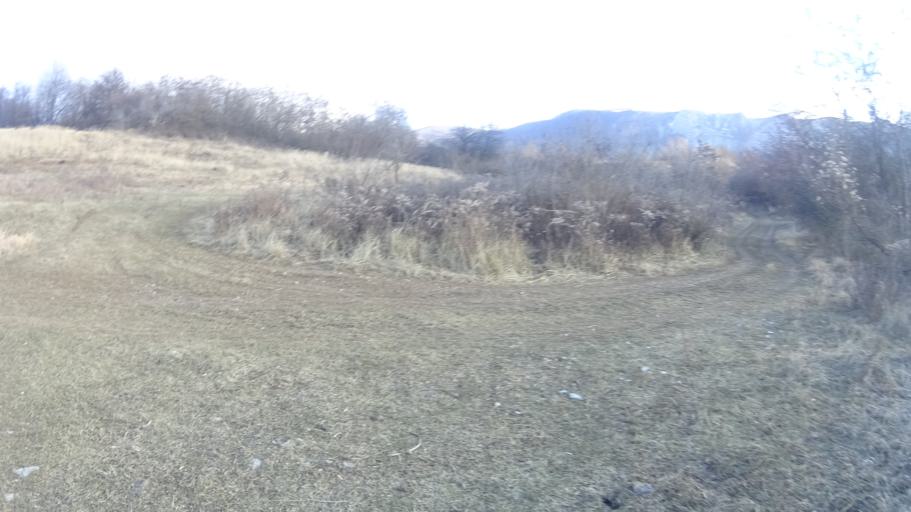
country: HU
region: Heves
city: Belapatfalva
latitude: 48.0622
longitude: 20.3593
